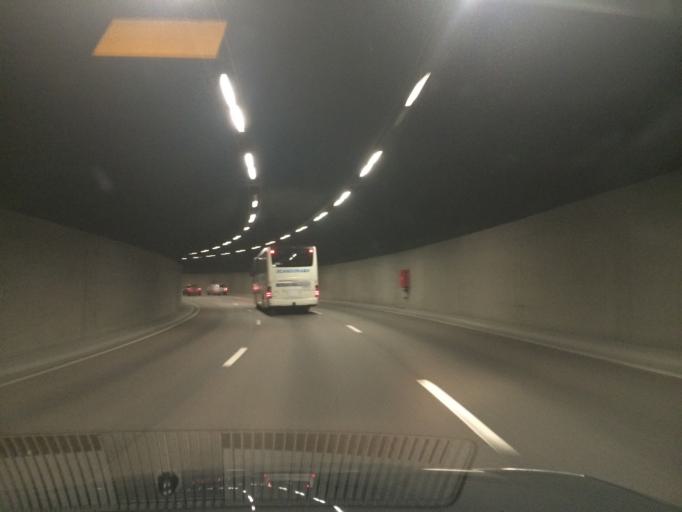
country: NO
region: Oslo
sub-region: Oslo
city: Oslo
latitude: 59.9057
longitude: 10.7862
